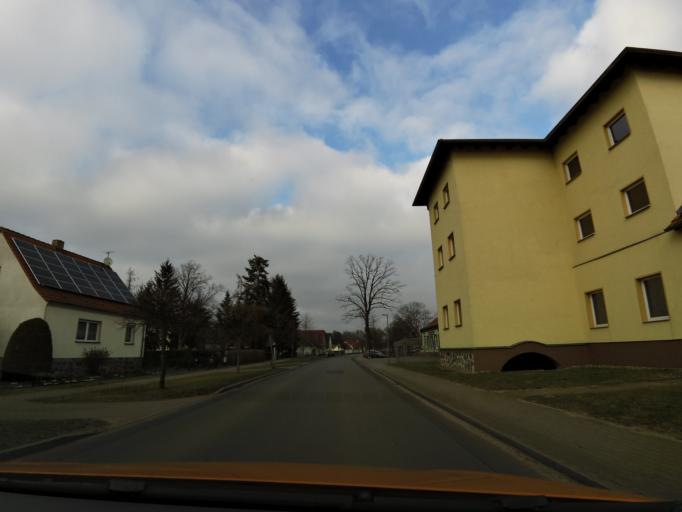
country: DE
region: Brandenburg
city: Walsleben
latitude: 52.9368
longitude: 12.6629
